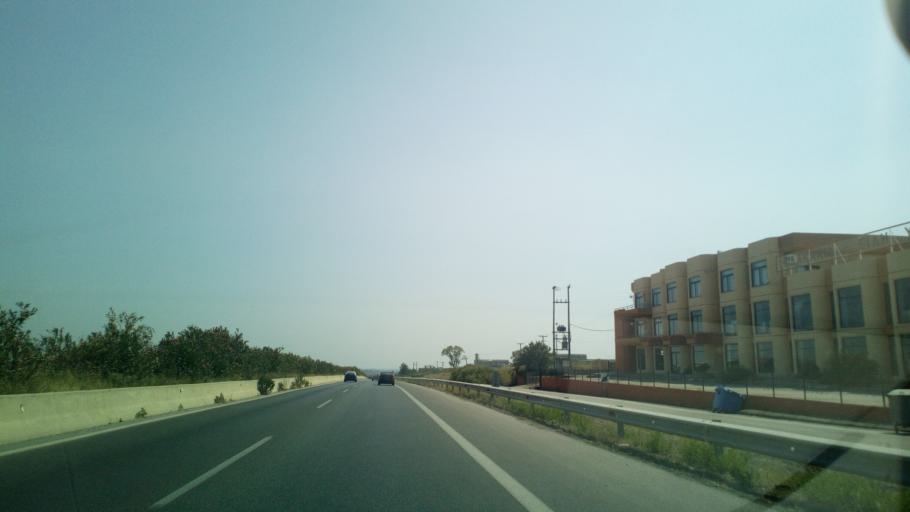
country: GR
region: Central Macedonia
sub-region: Nomos Chalkidikis
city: Lakkoma
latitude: 40.3924
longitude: 23.0346
